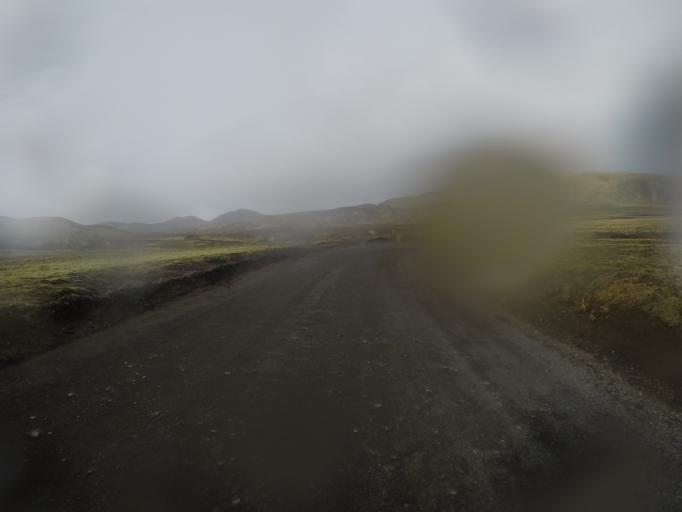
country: IS
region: South
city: Vestmannaeyjar
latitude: 63.9797
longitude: -18.8462
